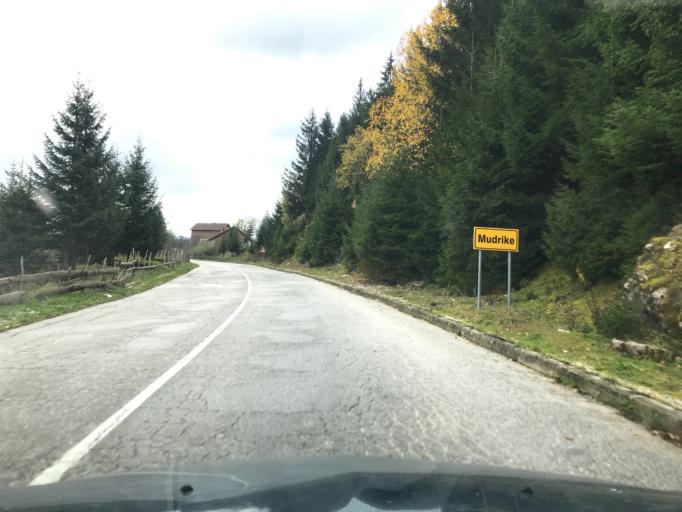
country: BA
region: Federation of Bosnia and Herzegovina
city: Turbe
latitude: 44.3149
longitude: 17.5170
